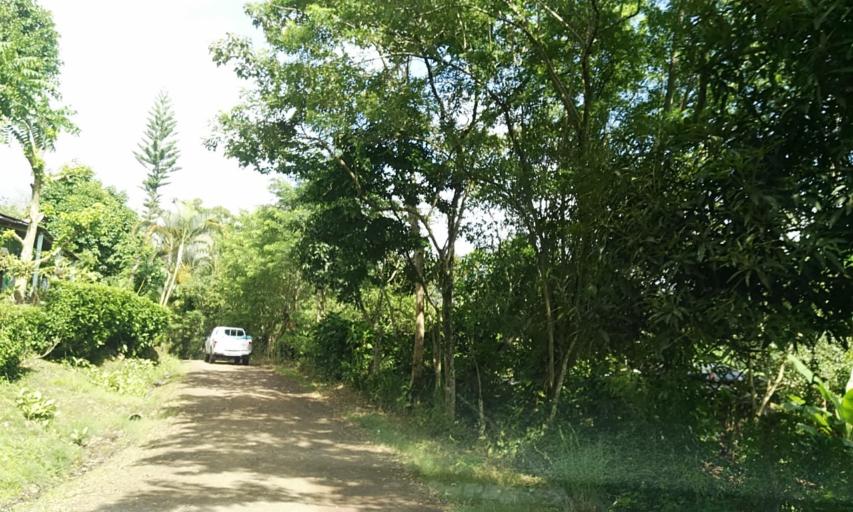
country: NI
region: Matagalpa
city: San Ramon
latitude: 12.9907
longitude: -85.8581
